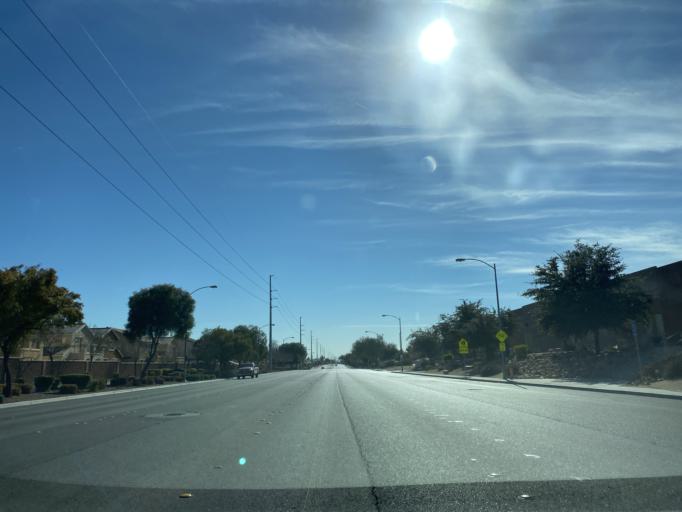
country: US
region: Nevada
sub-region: Clark County
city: North Las Vegas
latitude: 36.2682
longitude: -115.1440
